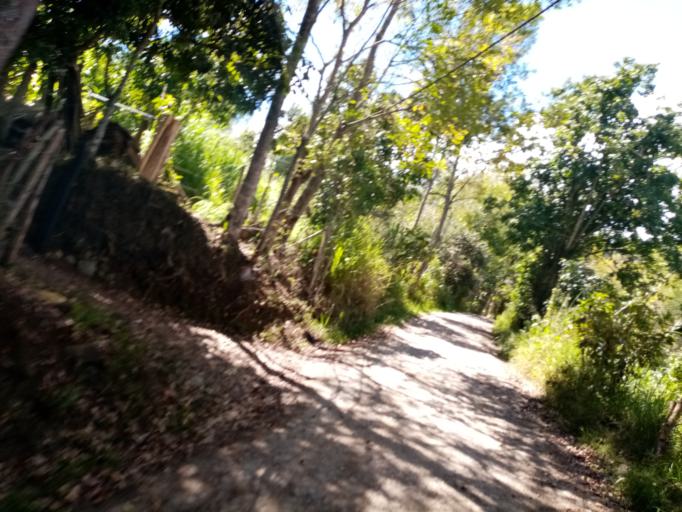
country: CO
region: Cundinamarca
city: Tenza
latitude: 5.0777
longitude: -73.4300
